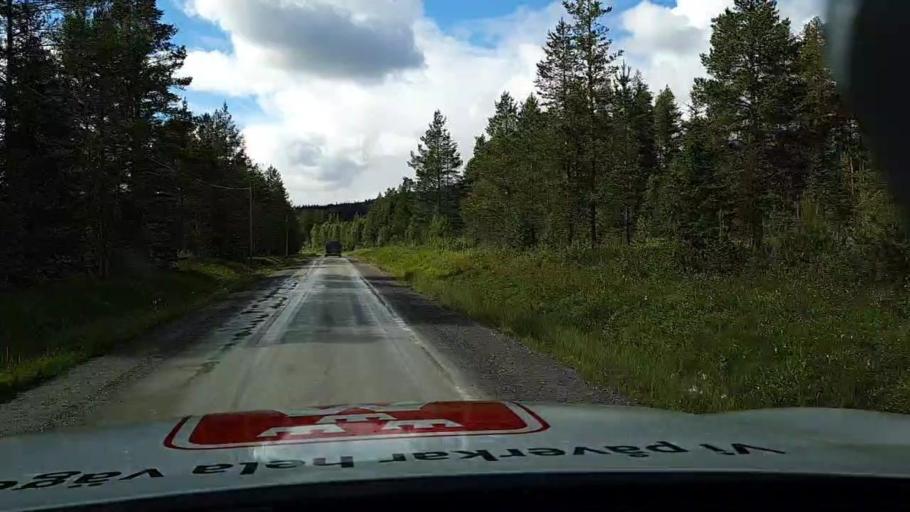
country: SE
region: Jaemtland
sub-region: Krokoms Kommun
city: Valla
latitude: 63.7101
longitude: 13.5466
